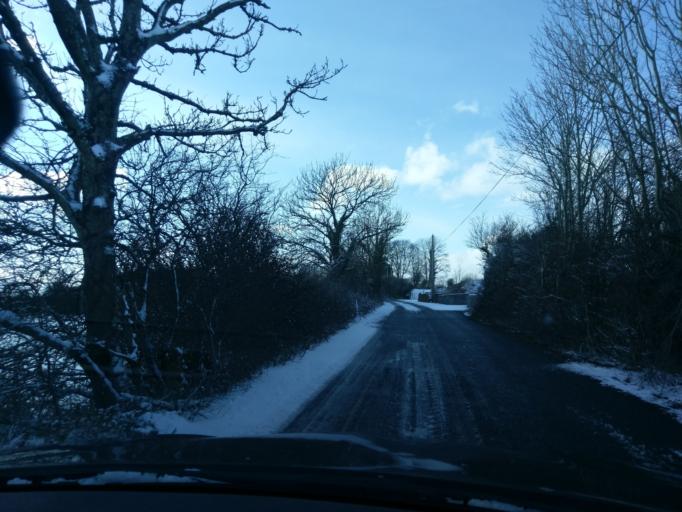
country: IE
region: Connaught
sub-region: County Galway
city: Athenry
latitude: 53.2040
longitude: -8.7734
